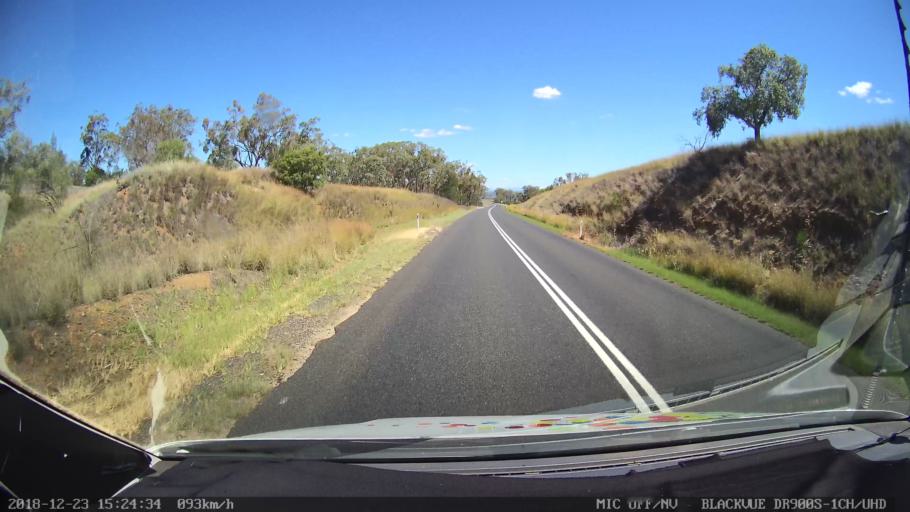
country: AU
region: New South Wales
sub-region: Tamworth Municipality
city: Manilla
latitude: -30.8934
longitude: 150.8241
